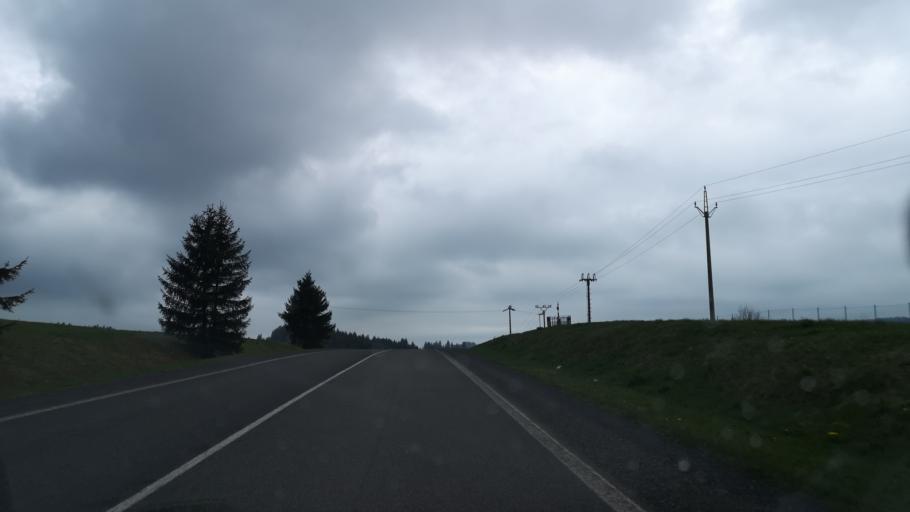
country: SK
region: Presovsky
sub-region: Okres Poprad
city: Strba
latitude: 49.0631
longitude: 19.9581
